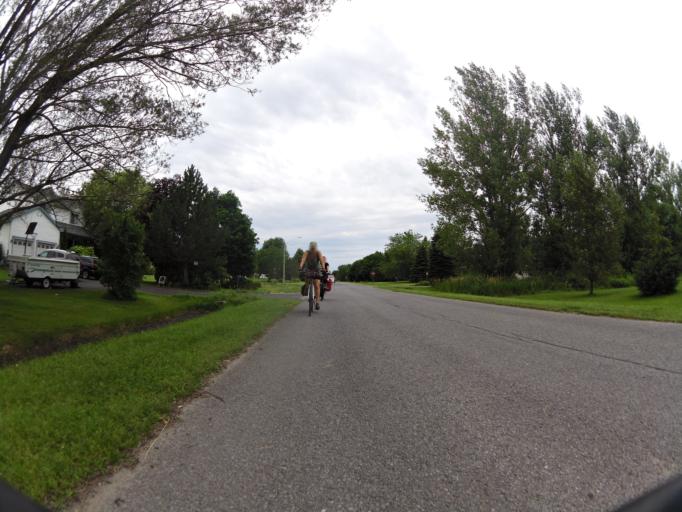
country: CA
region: Ontario
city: Bells Corners
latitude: 45.0260
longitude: -75.6888
